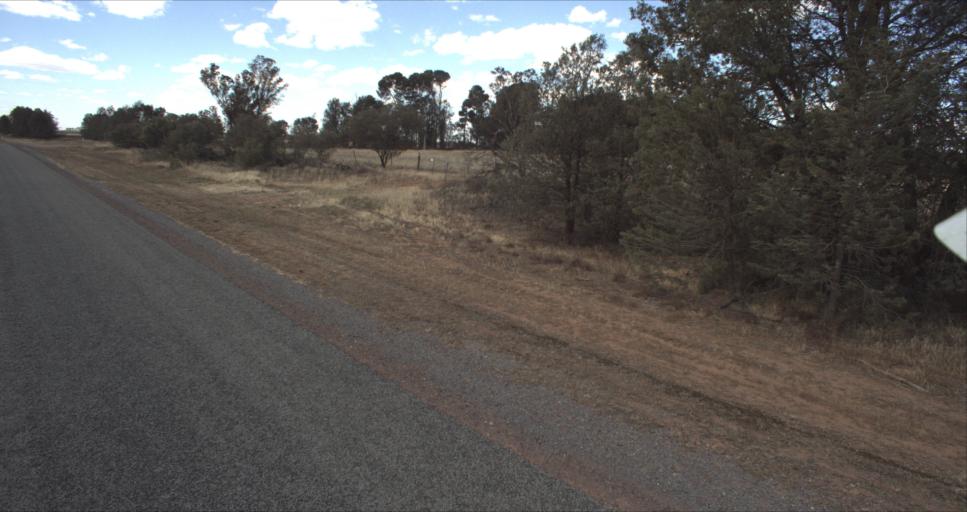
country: AU
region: New South Wales
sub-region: Leeton
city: Leeton
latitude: -34.4837
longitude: 146.2486
